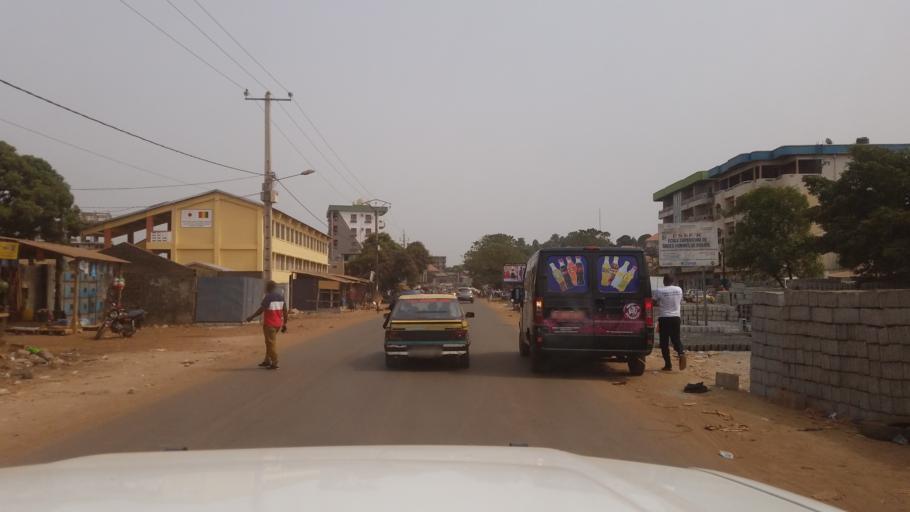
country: GN
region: Conakry
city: Conakry
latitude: 9.6534
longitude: -13.6014
